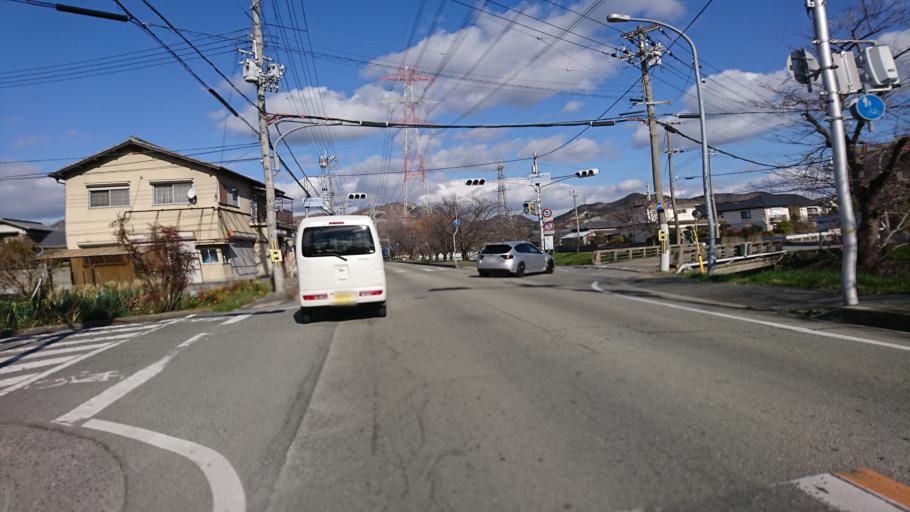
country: JP
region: Hyogo
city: Kakogawacho-honmachi
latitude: 34.7865
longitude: 134.7830
